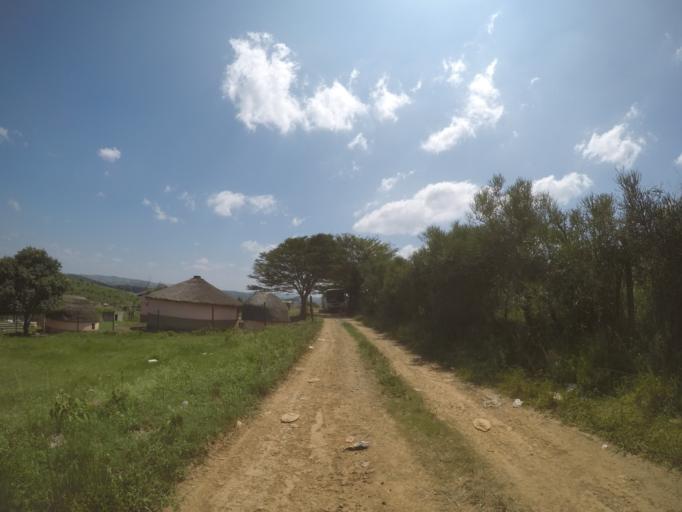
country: ZA
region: KwaZulu-Natal
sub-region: uThungulu District Municipality
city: Empangeni
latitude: -28.6009
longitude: 31.7406
